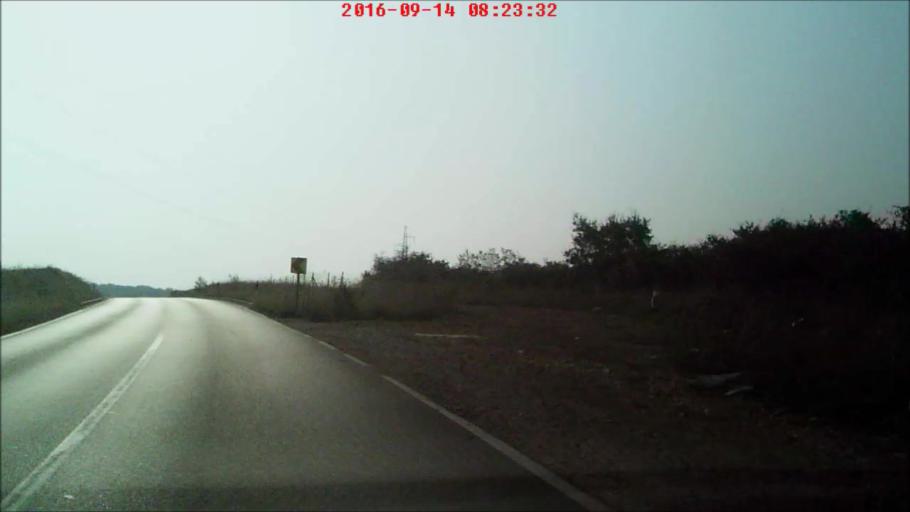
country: HR
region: Zadarska
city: Vrsi
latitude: 44.2116
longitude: 15.2322
